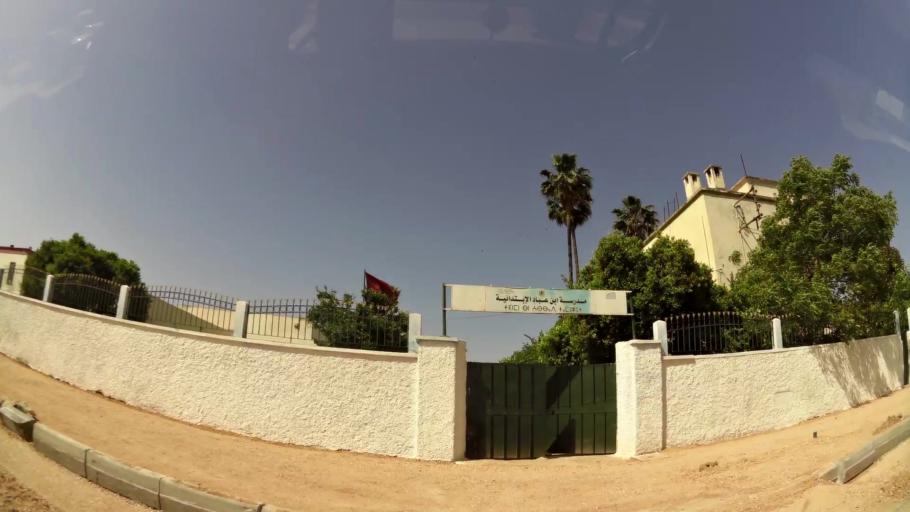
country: MA
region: Meknes-Tafilalet
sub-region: Meknes
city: Meknes
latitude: 33.8865
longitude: -5.5398
